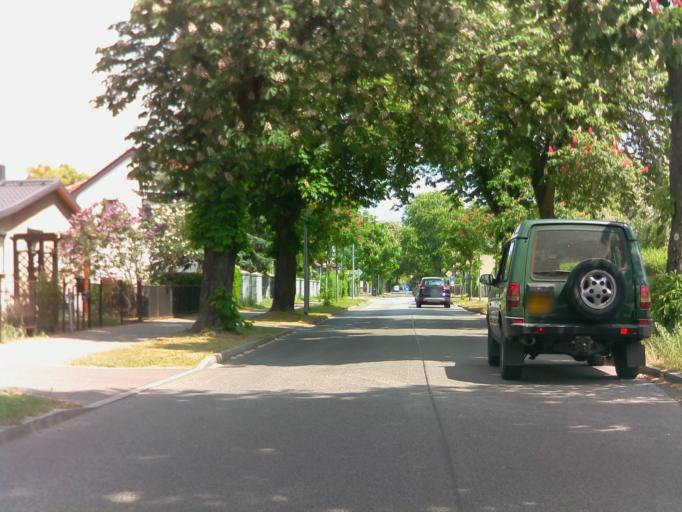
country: DE
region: Brandenburg
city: Dallgow-Doeberitz
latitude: 52.5506
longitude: 13.0688
